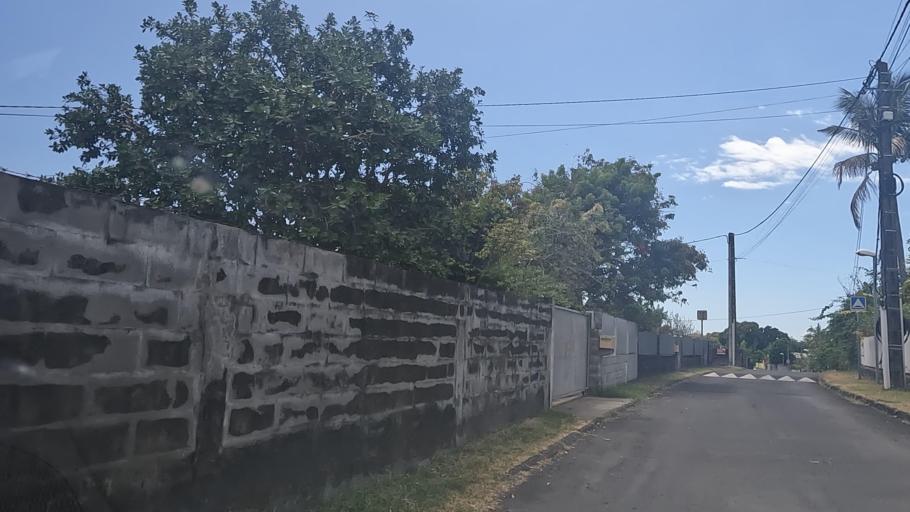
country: RE
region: Reunion
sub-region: Reunion
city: Saint-Benoit
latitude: -21.0317
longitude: 55.7035
